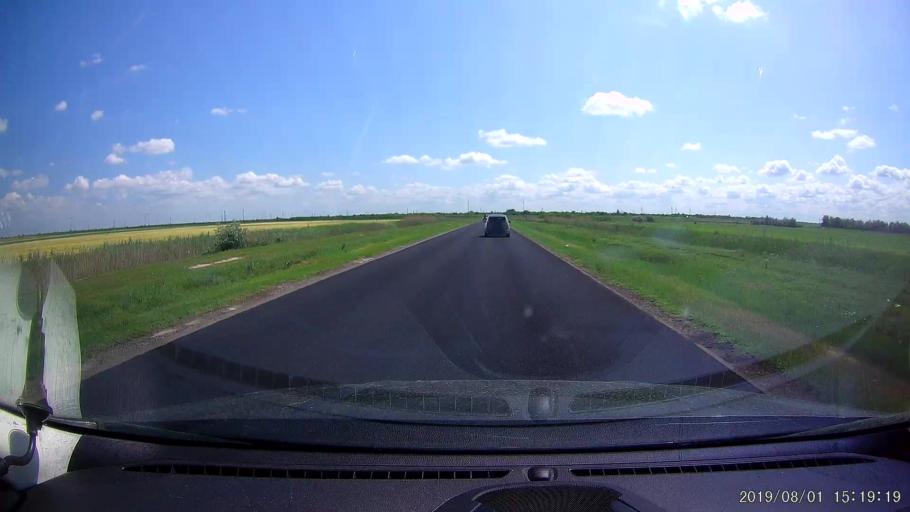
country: RO
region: Braila
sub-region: Comuna Unirea
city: Unirea
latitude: 45.0911
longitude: 27.8134
